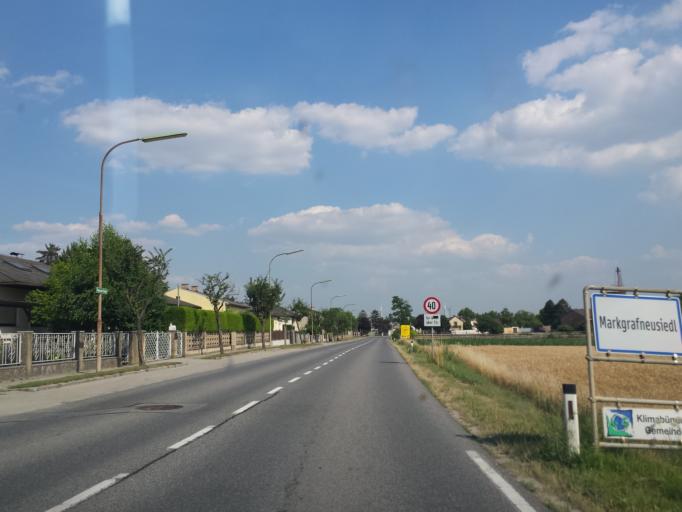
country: AT
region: Lower Austria
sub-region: Politischer Bezirk Ganserndorf
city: Markgrafneusiedl
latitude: 48.2713
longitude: 16.6251
